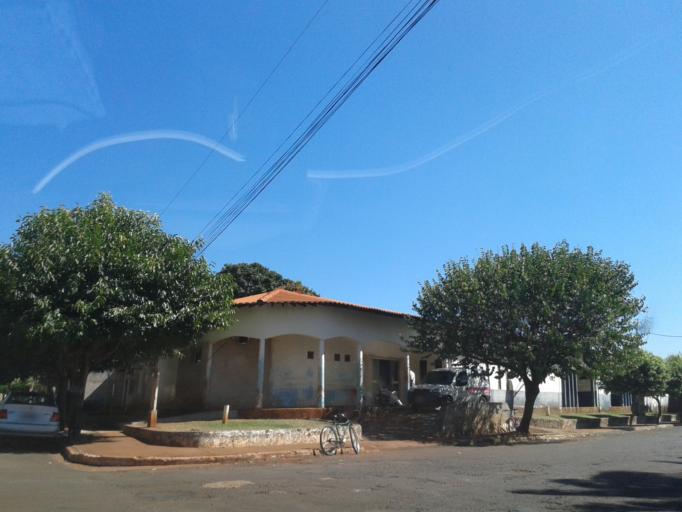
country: BR
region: Minas Gerais
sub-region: Capinopolis
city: Capinopolis
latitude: -18.5167
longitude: -49.5006
